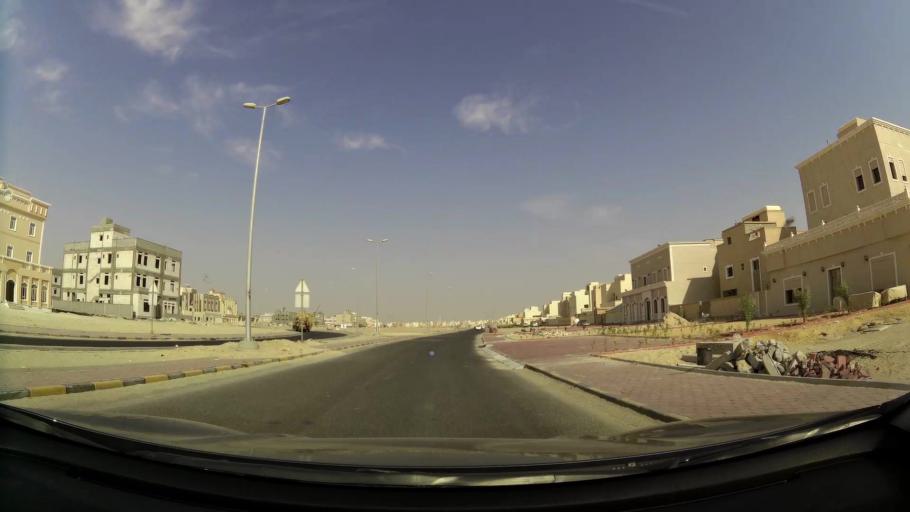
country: KW
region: Al Ahmadi
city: Al Wafrah
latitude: 28.7884
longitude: 48.0681
